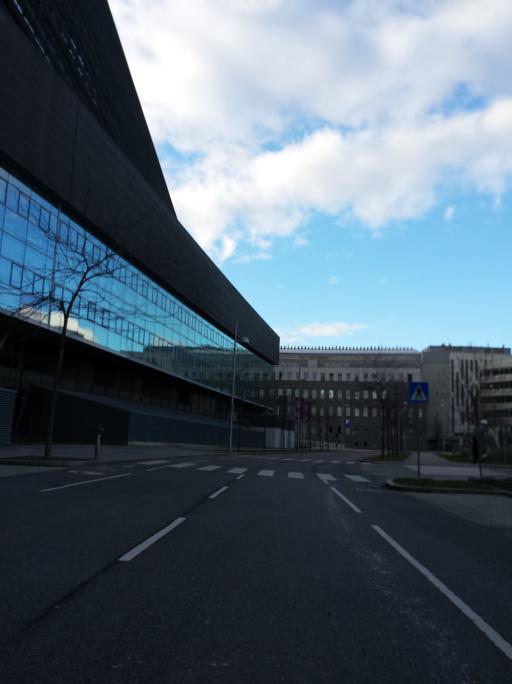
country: AT
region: Vienna
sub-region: Wien Stadt
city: Vienna
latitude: 48.1871
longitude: 16.4037
